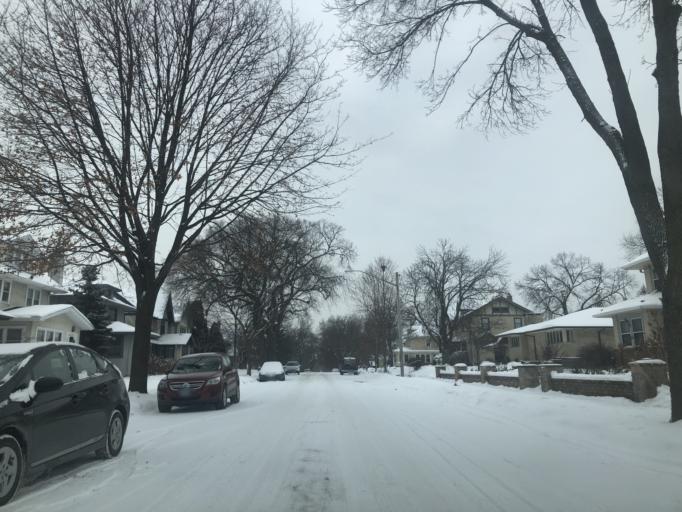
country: US
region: Minnesota
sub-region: Hennepin County
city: Richfield
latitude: 44.9277
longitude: -93.2870
